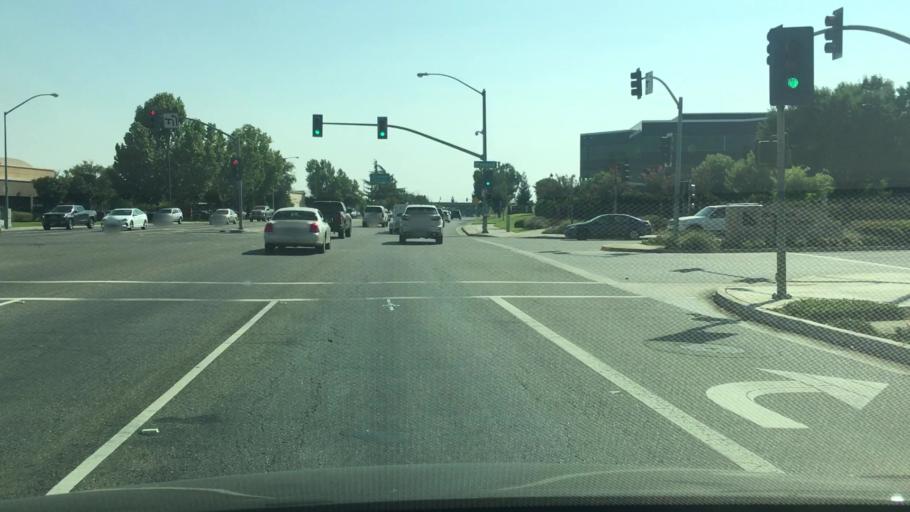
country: US
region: California
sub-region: Fresno County
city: Clovis
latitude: 36.8577
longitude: -119.7850
